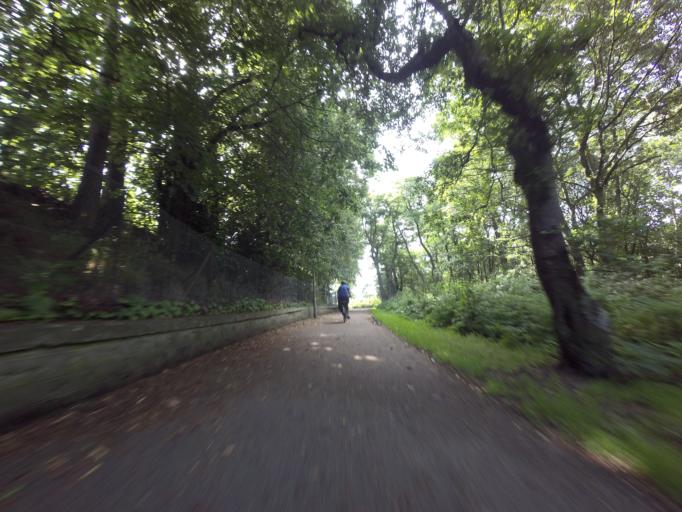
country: GB
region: Scotland
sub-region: Highland
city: Nairn
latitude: 57.5813
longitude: -3.8633
